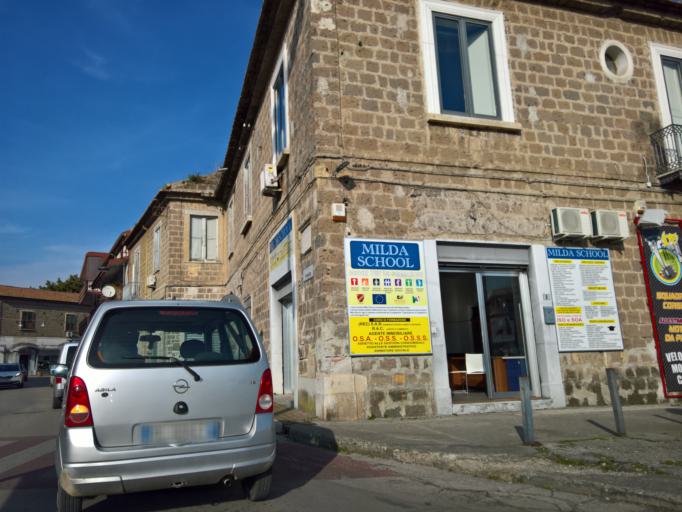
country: IT
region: Campania
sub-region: Provincia di Caserta
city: San Prisco
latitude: 41.0821
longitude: 14.2698
